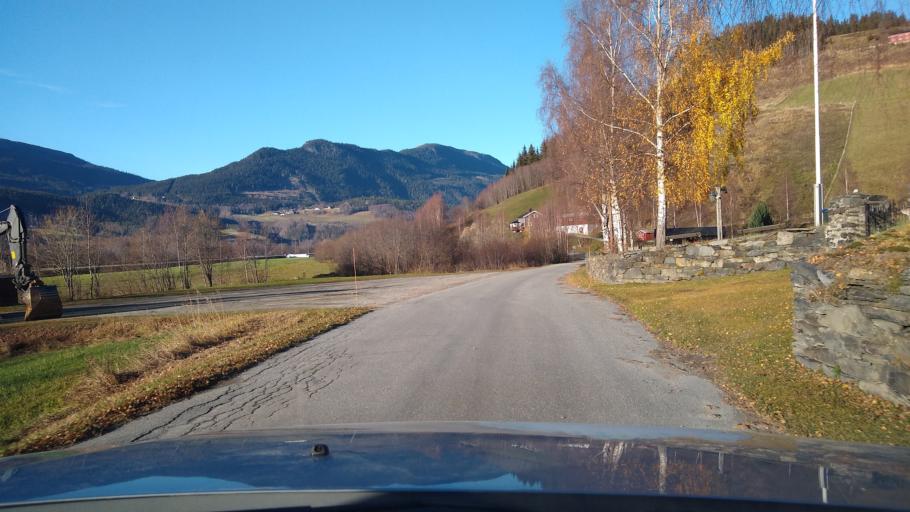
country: NO
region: Oppland
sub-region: Ringebu
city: Ringebu
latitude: 61.4268
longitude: 10.2201
